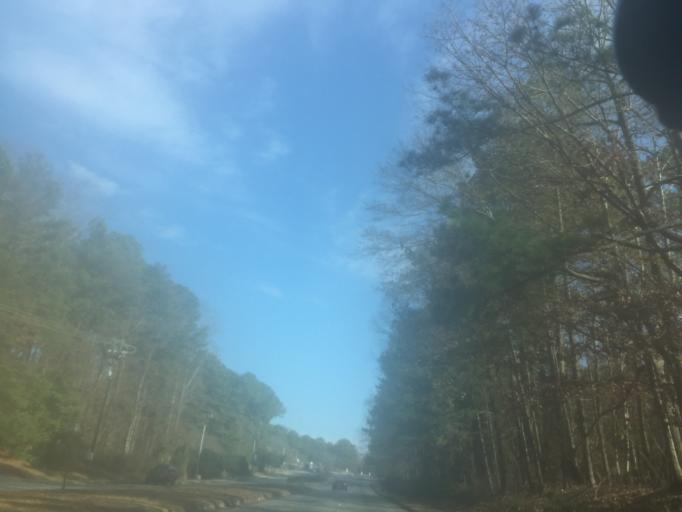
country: US
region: Georgia
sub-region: Clayton County
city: Riverdale
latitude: 33.5959
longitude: -84.4197
